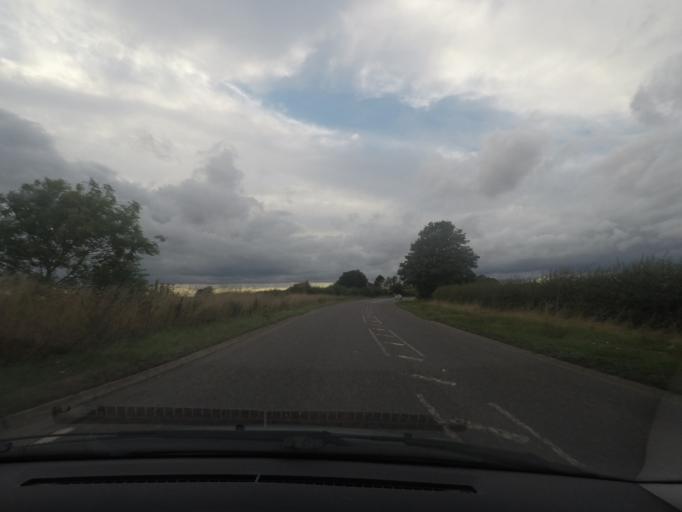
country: GB
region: England
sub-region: Lincolnshire
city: Burwell
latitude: 53.2701
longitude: 0.0710
